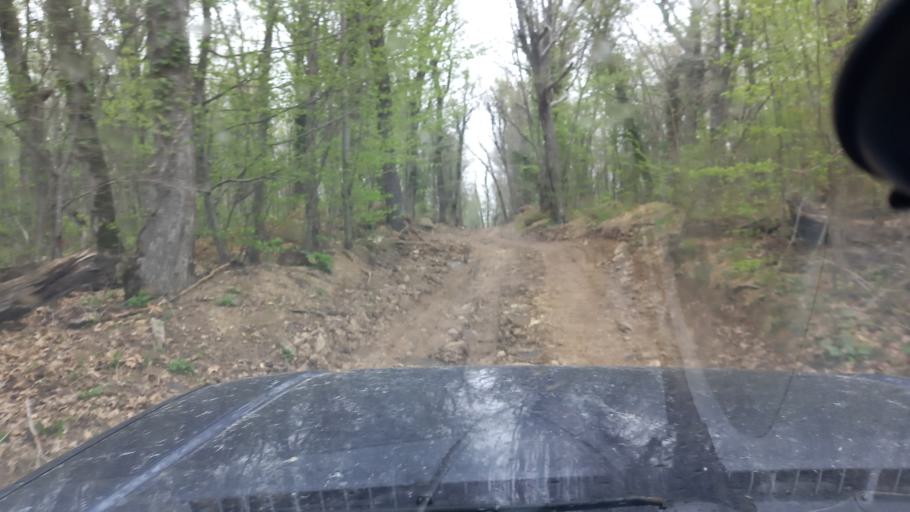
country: RU
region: Krasnodarskiy
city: Dzhubga
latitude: 44.3124
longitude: 38.6798
